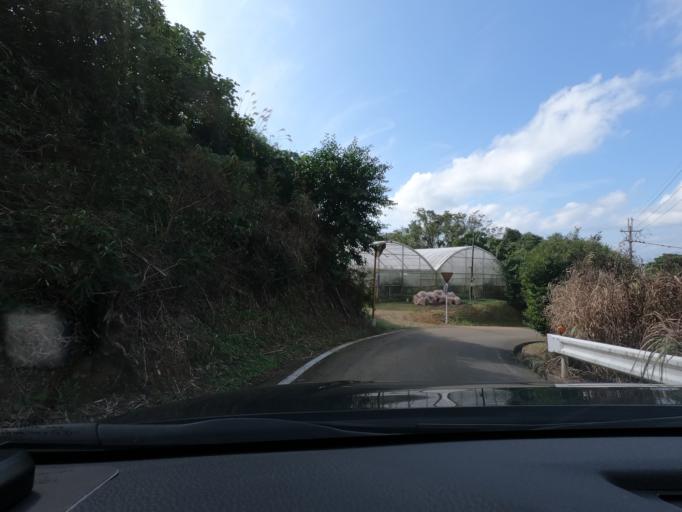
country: JP
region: Okinawa
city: Nago
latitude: 26.7569
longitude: 128.1977
